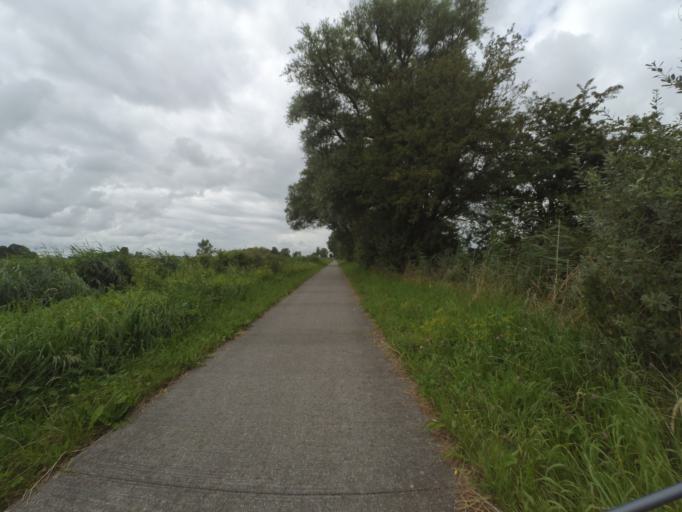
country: NL
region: Friesland
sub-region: Gemeente Dongeradeel
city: Anjum
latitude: 53.3218
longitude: 6.1080
